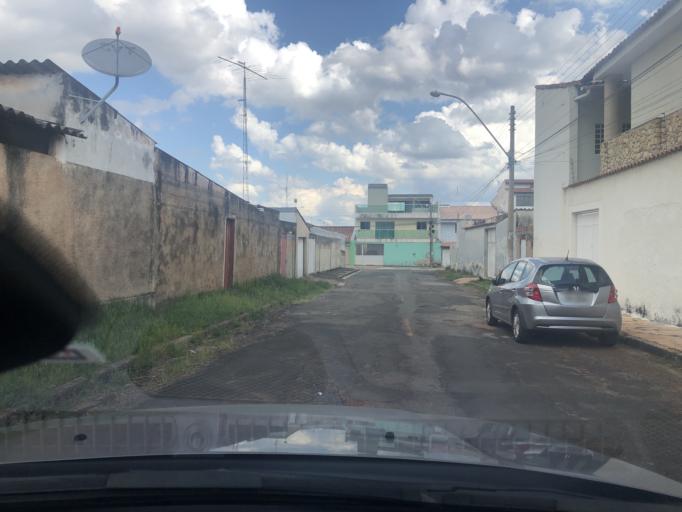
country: BR
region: Goias
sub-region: Luziania
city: Luziania
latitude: -16.0251
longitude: -48.0621
